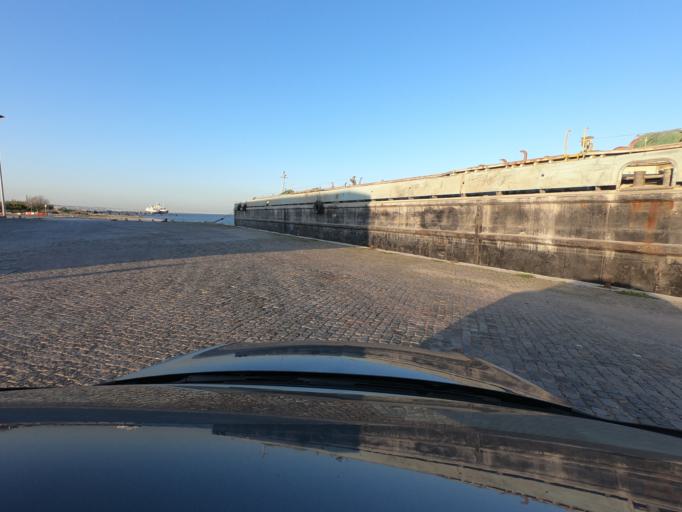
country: PT
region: Lisbon
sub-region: Loures
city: Moscavide
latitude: 38.7418
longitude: -9.0982
